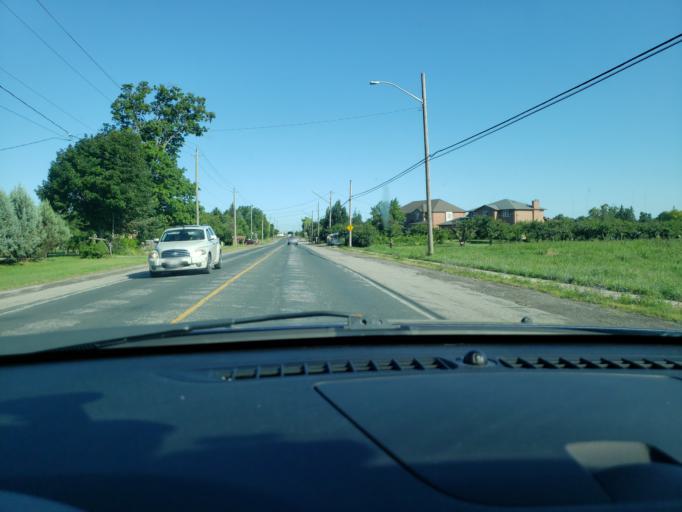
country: CA
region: Ontario
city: Hamilton
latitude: 43.1975
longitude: -79.6057
